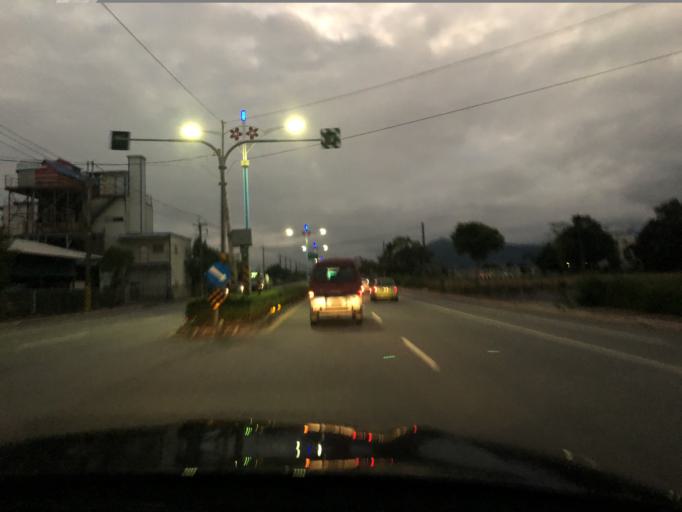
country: TW
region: Taiwan
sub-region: Hualien
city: Hualian
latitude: 23.9691
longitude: 121.5699
